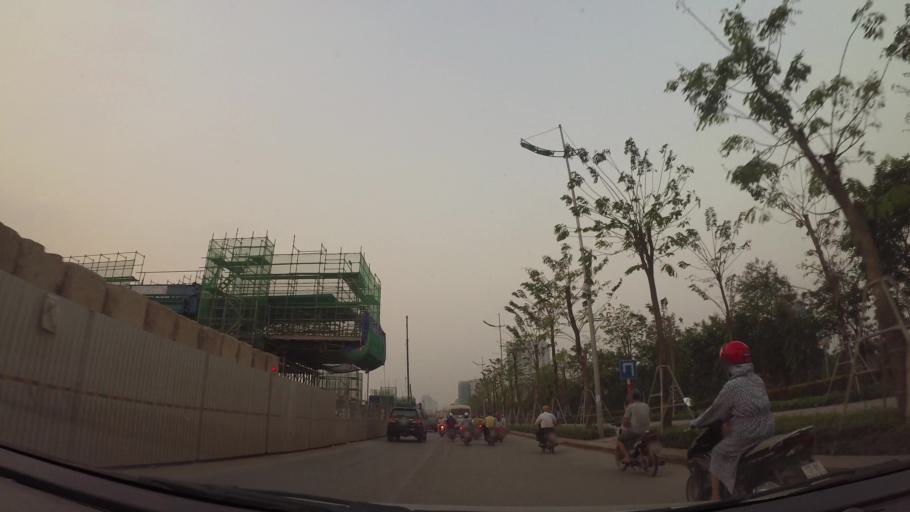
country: VN
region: Ha Noi
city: Tay Ho
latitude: 21.0647
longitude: 105.7847
